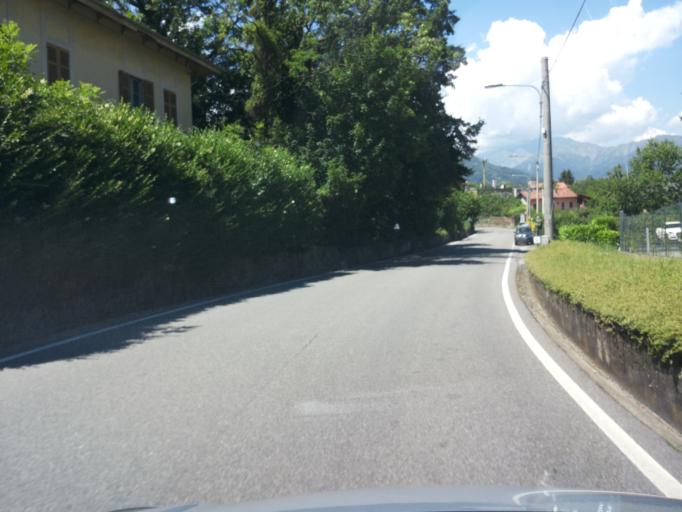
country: IT
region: Piedmont
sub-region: Provincia di Biella
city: Pralungo
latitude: 45.5817
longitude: 8.0381
